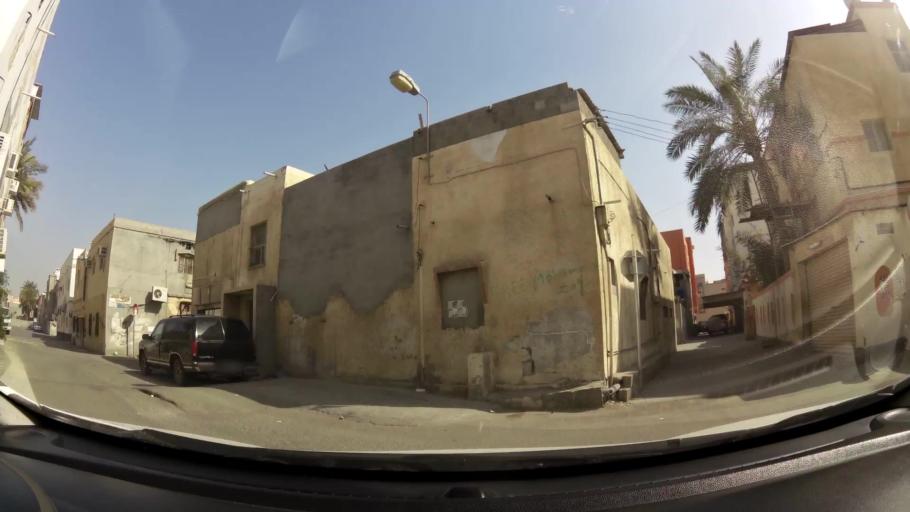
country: BH
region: Manama
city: Jidd Hafs
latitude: 26.2100
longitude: 50.4579
